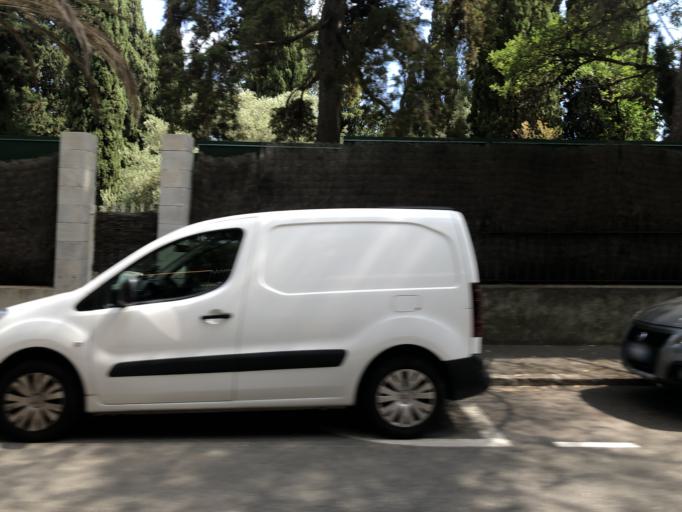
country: FR
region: Provence-Alpes-Cote d'Azur
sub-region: Departement des Alpes-Maritimes
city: Eze
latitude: 43.7182
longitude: 7.3499
